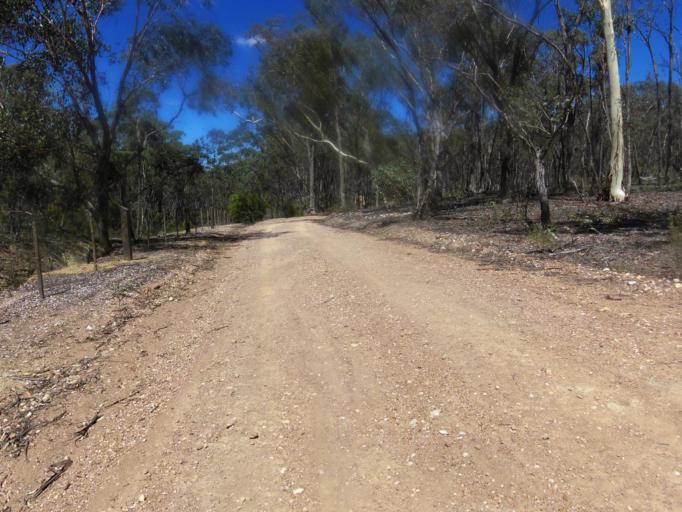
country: AU
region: Victoria
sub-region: Mount Alexander
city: Castlemaine
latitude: -37.0550
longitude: 144.1885
